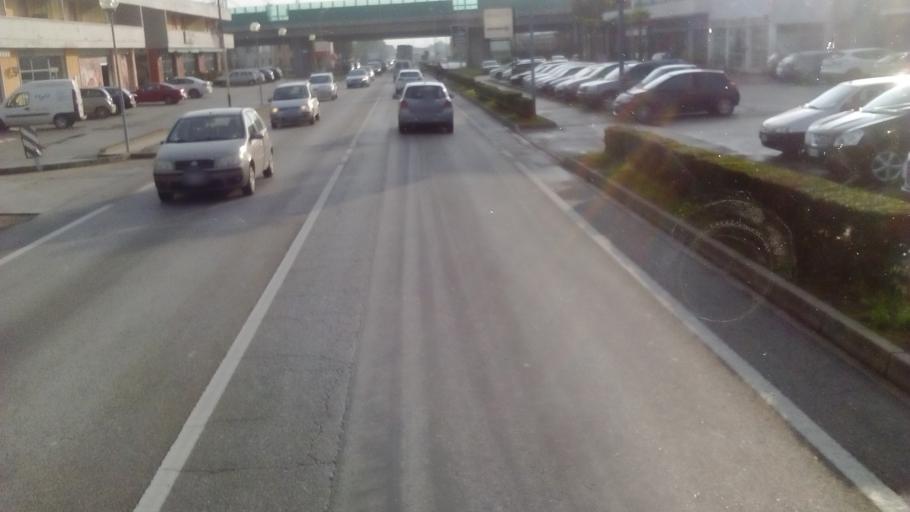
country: IT
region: Veneto
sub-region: Provincia di Vicenza
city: Dueville
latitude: 45.6404
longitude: 11.5746
